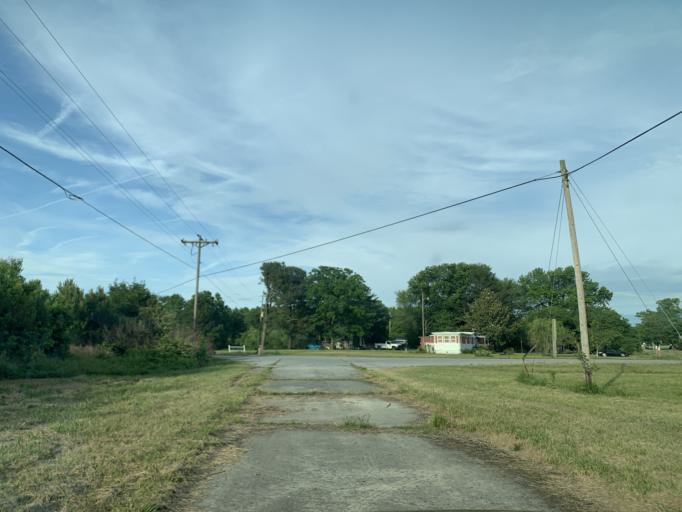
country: US
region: Maryland
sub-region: Worcester County
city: Pocomoke City
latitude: 38.0740
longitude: -75.4803
